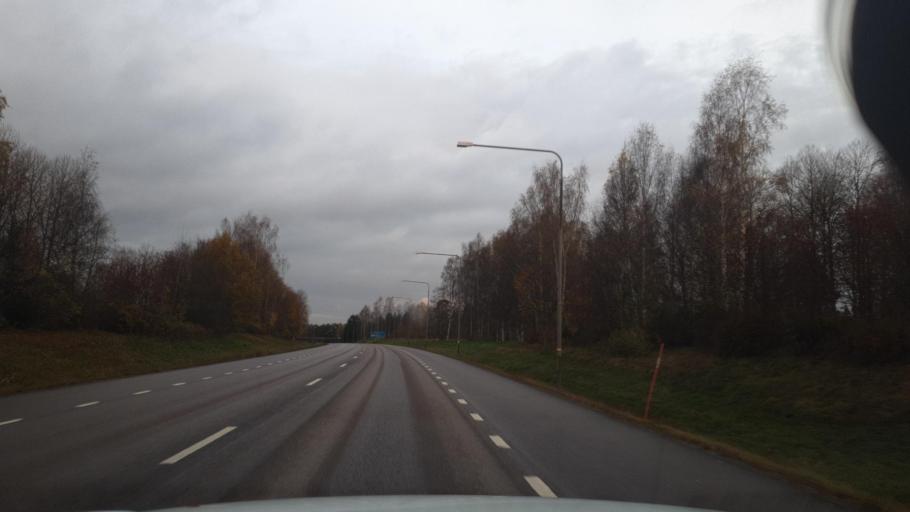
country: SE
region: Vaermland
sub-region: Arvika Kommun
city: Arvika
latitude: 59.6682
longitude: 12.6053
